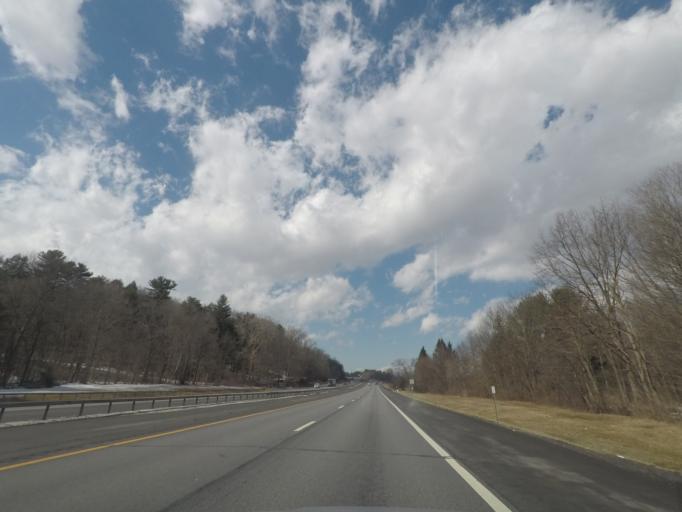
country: US
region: New York
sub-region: Montgomery County
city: Hagaman
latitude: 42.8880
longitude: -74.0798
